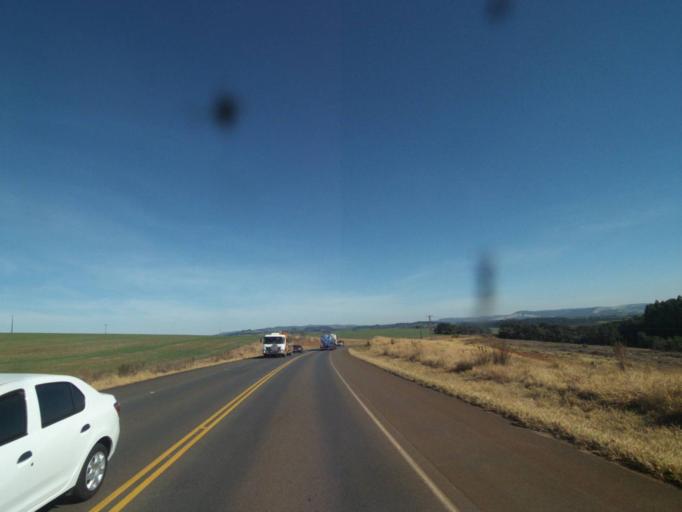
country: BR
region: Parana
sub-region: Tibagi
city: Tibagi
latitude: -24.4580
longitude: -50.4246
